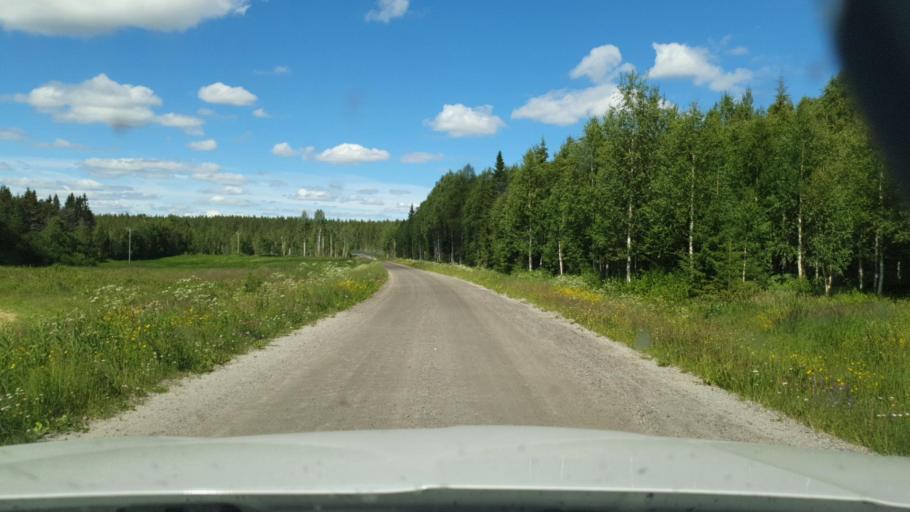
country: SE
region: Vaesterbotten
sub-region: Skelleftea Kommun
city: Backa
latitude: 65.1570
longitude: 21.1593
